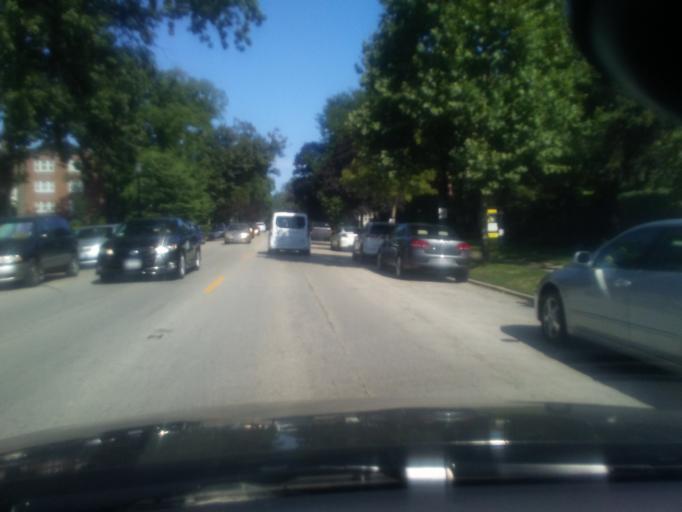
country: US
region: Illinois
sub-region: Cook County
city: Wilmette
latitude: 42.0644
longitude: -87.7124
